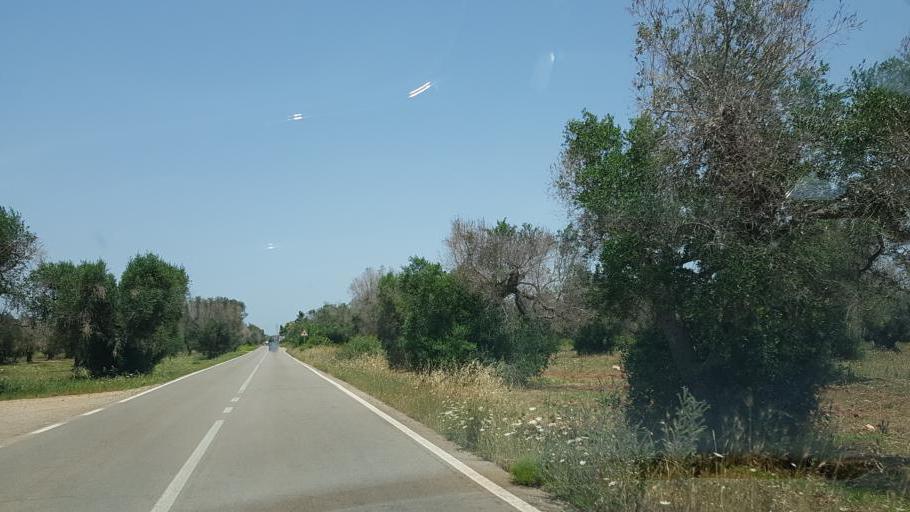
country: IT
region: Apulia
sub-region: Provincia di Lecce
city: Veglie
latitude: 40.3220
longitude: 17.9242
